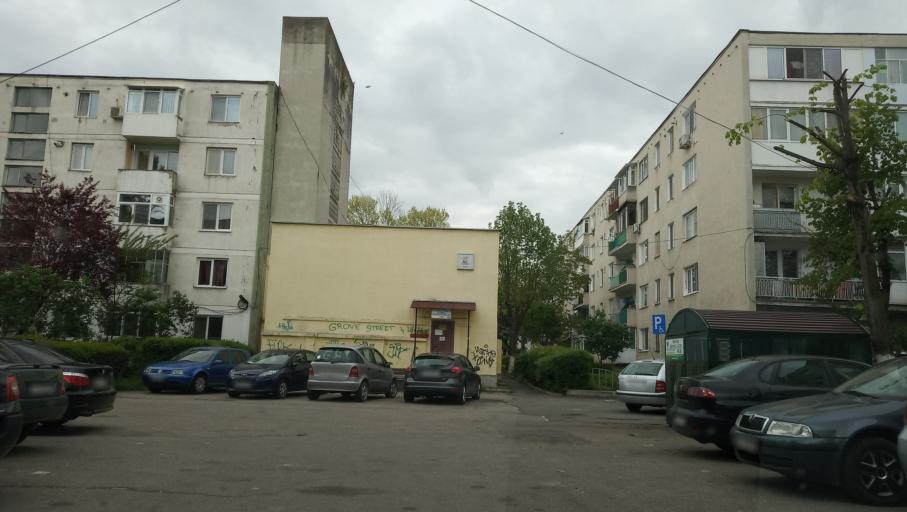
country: RO
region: Valcea
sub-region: Municipiul Ramnicu Valcea
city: Ramnicu Valcea
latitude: 45.0993
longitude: 24.3650
